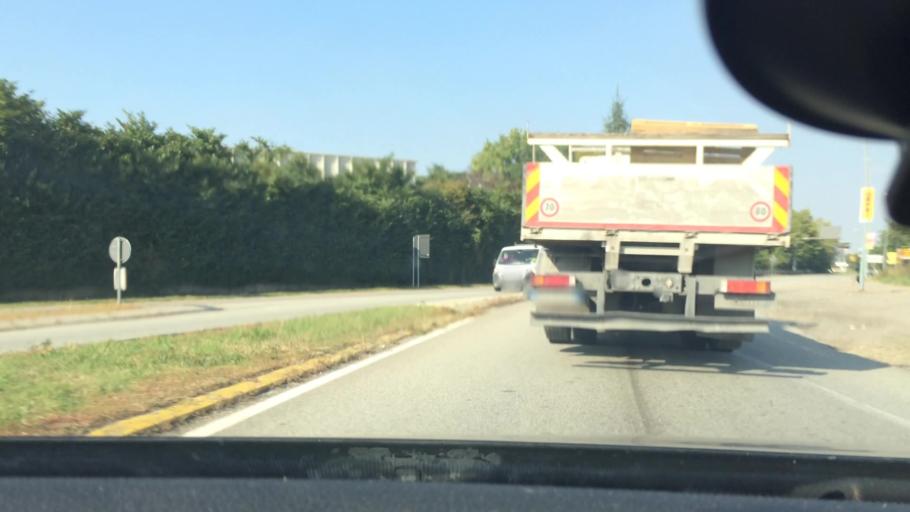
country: IT
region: Lombardy
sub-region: Citta metropolitana di Milano
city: Arluno
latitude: 45.4943
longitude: 8.9344
